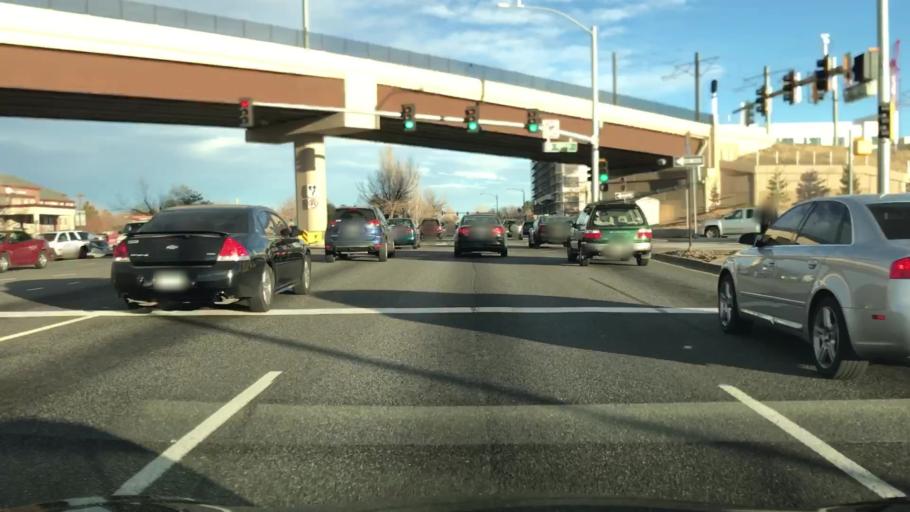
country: US
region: Colorado
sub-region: Adams County
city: Aurora
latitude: 39.6748
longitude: -104.8272
